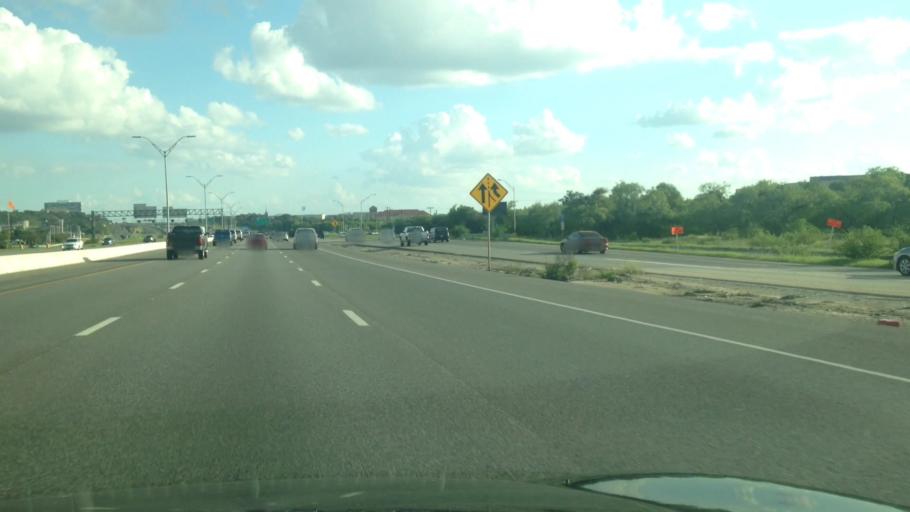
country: US
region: Texas
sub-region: Bexar County
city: Shavano Park
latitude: 29.5883
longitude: -98.5982
